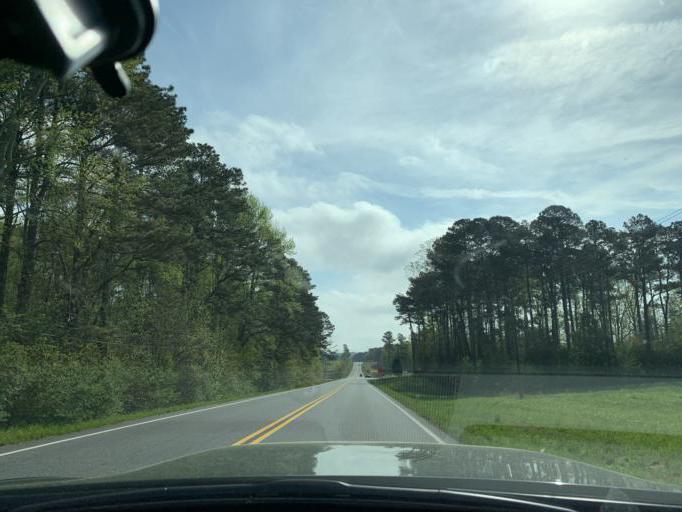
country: US
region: Georgia
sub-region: Forsyth County
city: Cumming
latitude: 34.2501
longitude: -84.1070
